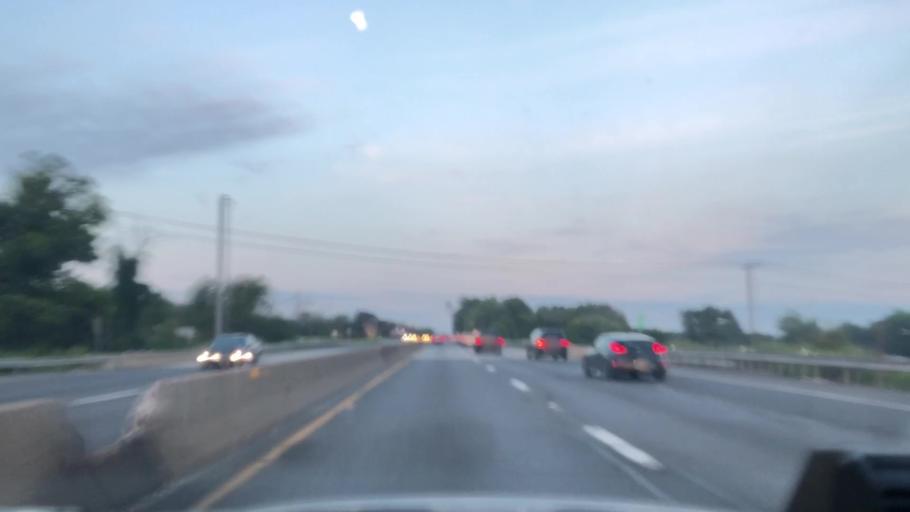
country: US
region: Pennsylvania
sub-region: Lehigh County
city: Allentown
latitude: 40.6185
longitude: -75.5003
